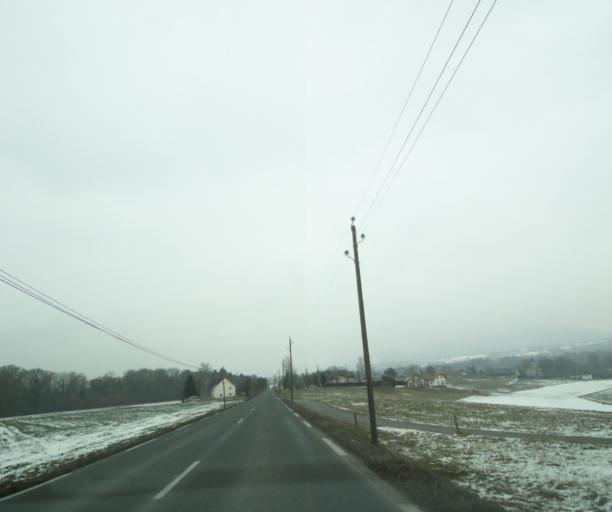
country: FR
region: Rhone-Alpes
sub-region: Departement de la Haute-Savoie
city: Contamine-sur-Arve
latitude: 46.1269
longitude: 6.3134
